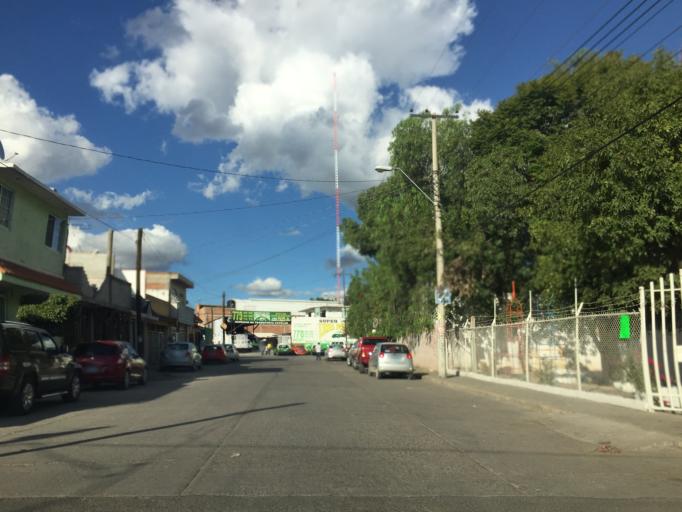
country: MX
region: Guanajuato
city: Leon
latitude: 21.1022
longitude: -101.7002
